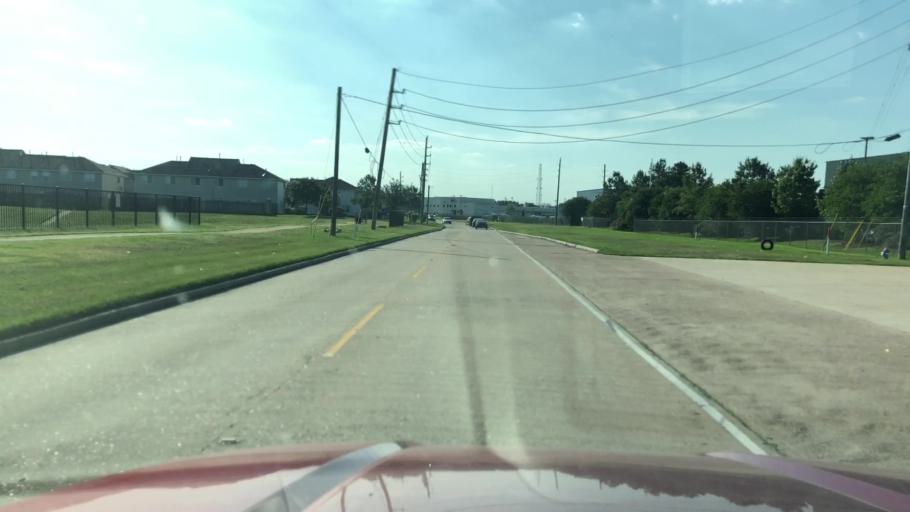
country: US
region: Texas
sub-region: Harris County
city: Hudson
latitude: 29.9445
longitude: -95.4930
